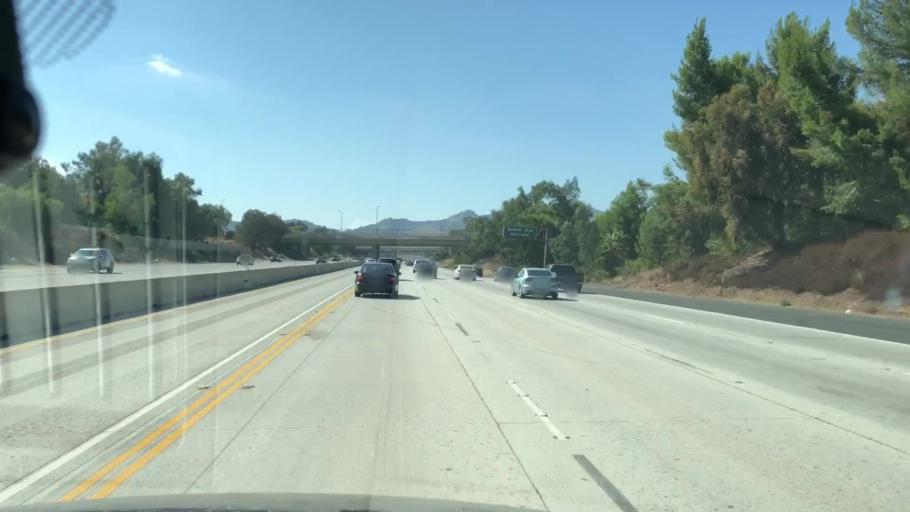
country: US
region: California
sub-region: Los Angeles County
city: Chatsworth
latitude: 34.2736
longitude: -118.5763
